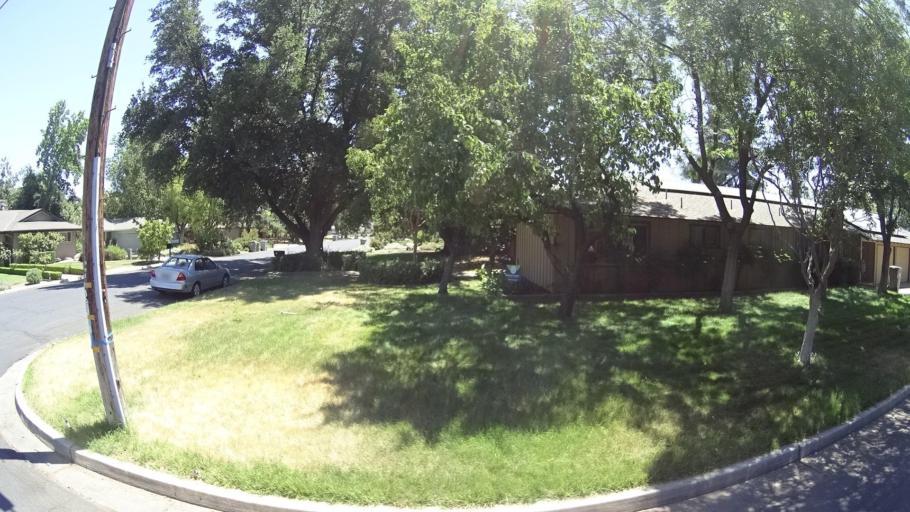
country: US
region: California
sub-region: Fresno County
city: Fresno
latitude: 36.7957
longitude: -119.7950
